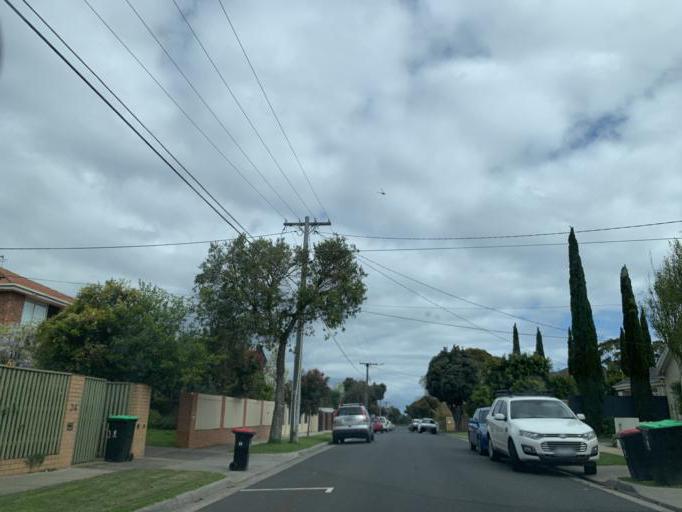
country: AU
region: Victoria
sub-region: Kingston
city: Mentone
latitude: -37.9839
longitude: 145.0551
